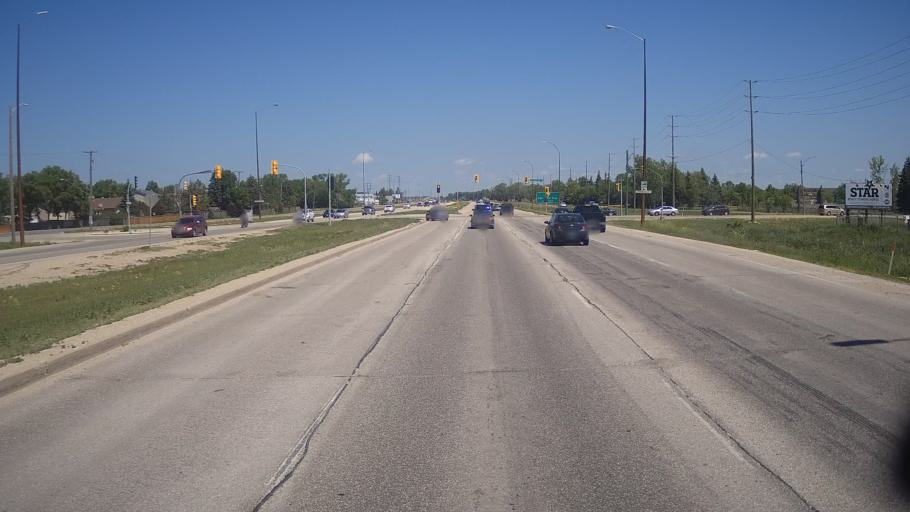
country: CA
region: Manitoba
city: Winnipeg
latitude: 49.9303
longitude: -97.0452
